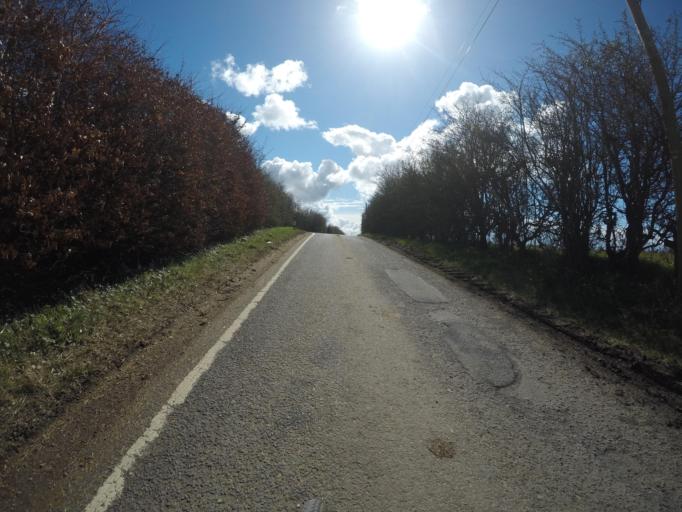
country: GB
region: Scotland
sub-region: North Ayrshire
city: Kilwinning
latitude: 55.6695
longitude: -4.7204
